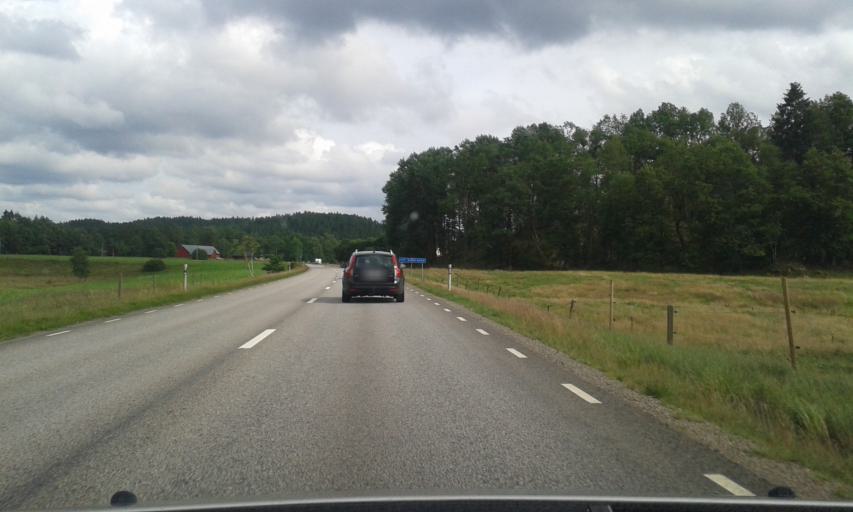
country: SE
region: Vaestra Goetaland
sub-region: Marks Kommun
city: Horred
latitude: 57.1502
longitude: 12.6813
